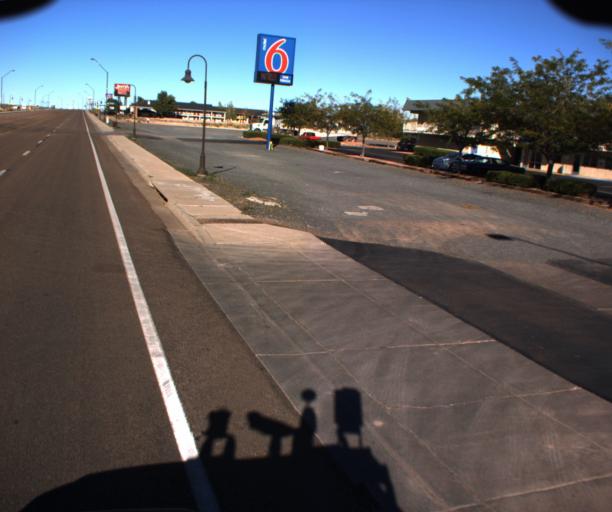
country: US
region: Arizona
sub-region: Navajo County
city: Holbrook
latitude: 34.9332
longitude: -110.1362
